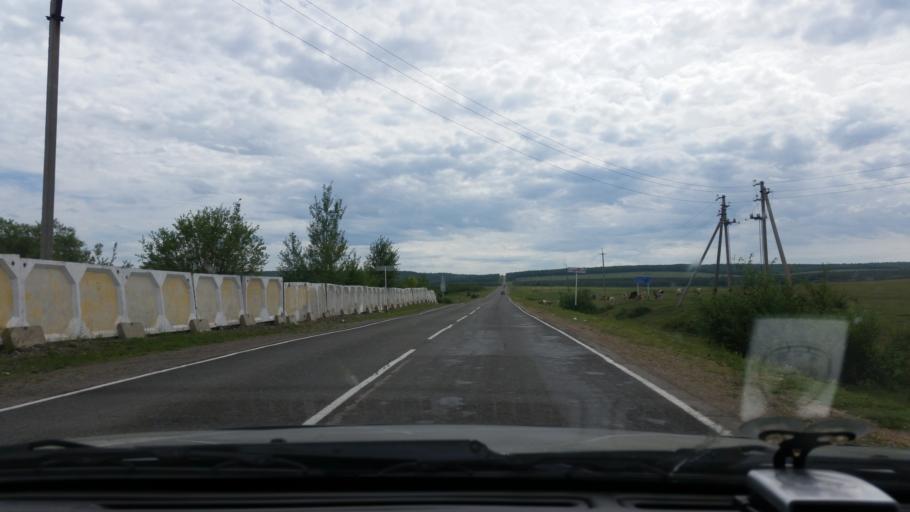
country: RU
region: Irkutsk
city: Bayanday
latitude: 53.0524
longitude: 105.5274
